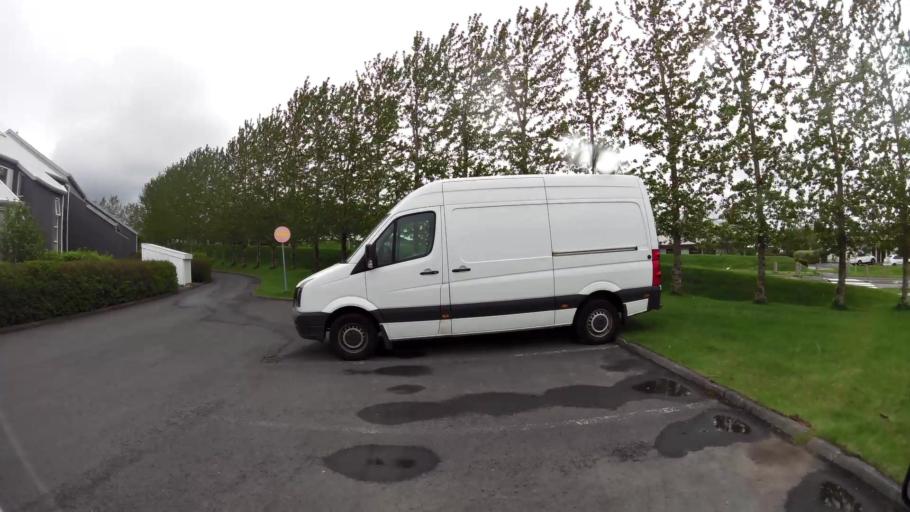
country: IS
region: Capital Region
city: Gardabaer
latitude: 64.0925
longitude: -21.9295
